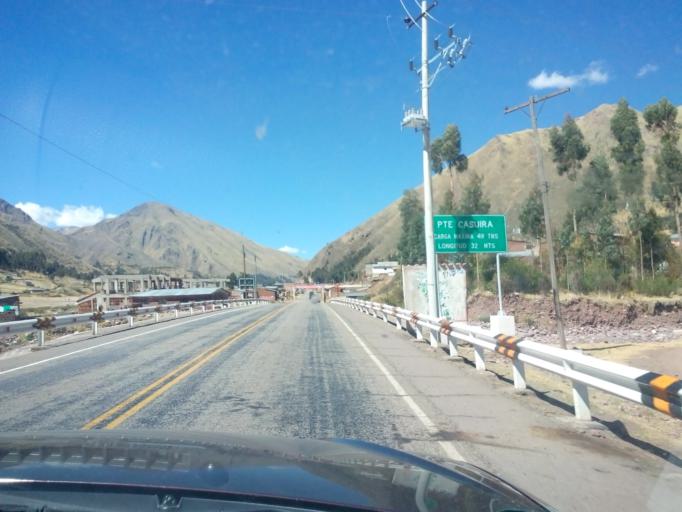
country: PE
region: Cusco
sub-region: Provincia de Canchis
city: Marangani
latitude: -14.3540
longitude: -71.1695
